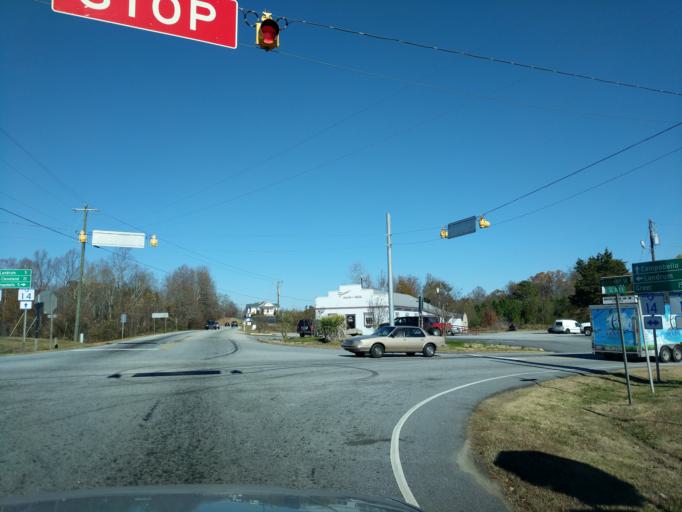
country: US
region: South Carolina
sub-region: Spartanburg County
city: Landrum
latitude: 35.1140
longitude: -82.2252
